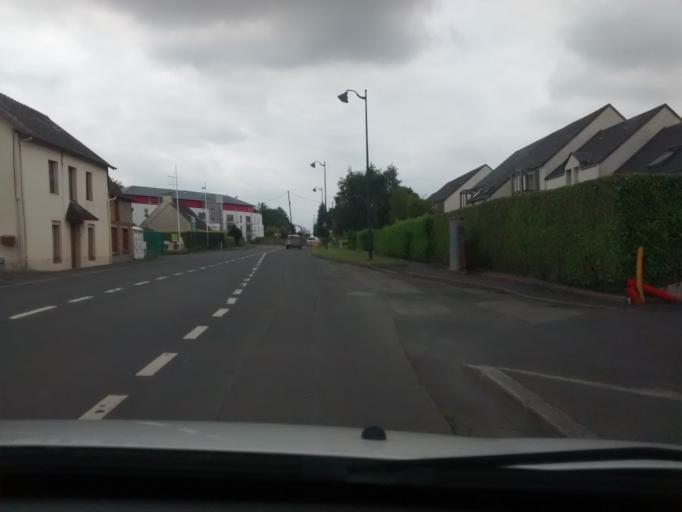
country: FR
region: Brittany
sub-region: Departement d'Ille-et-Vilaine
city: Liffre
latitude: 48.2099
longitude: -1.5157
